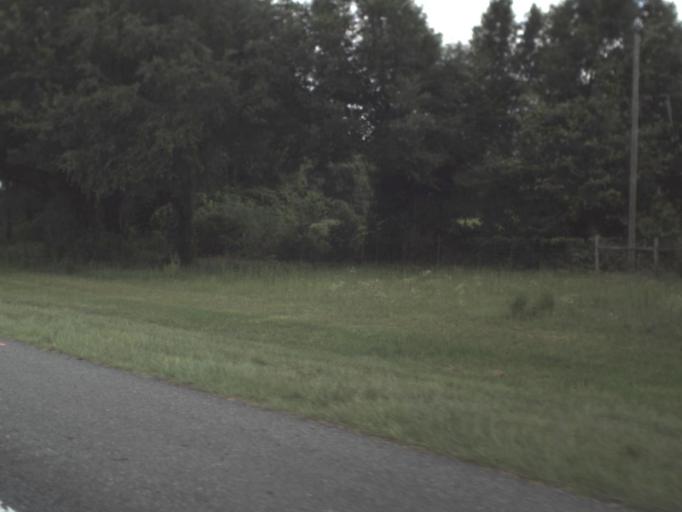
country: US
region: Florida
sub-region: Suwannee County
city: Wellborn
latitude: 30.2363
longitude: -82.7339
